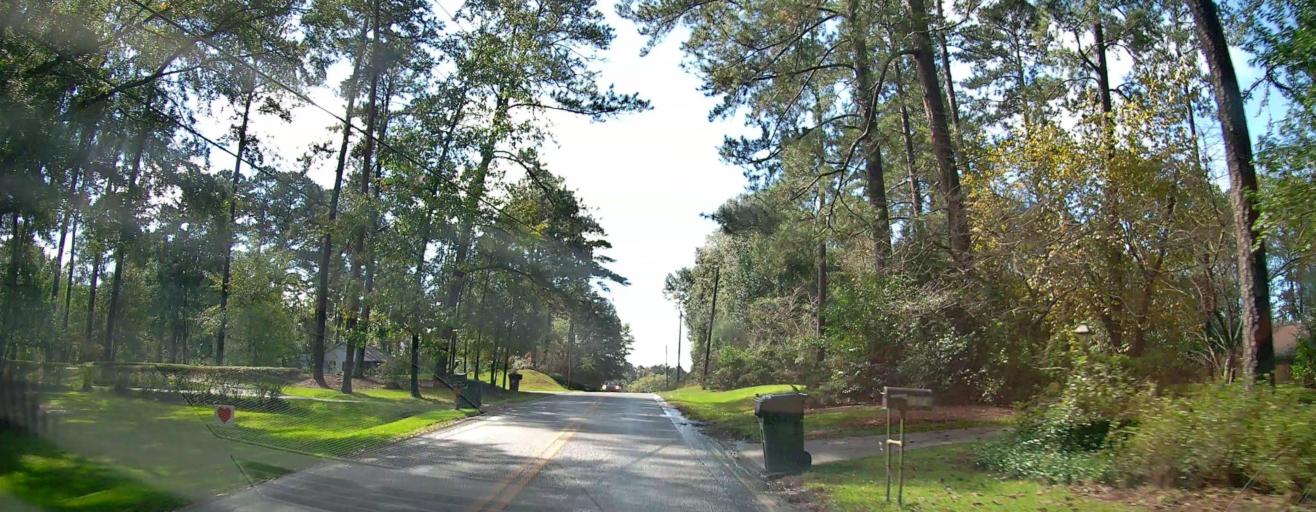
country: US
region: Georgia
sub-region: Bibb County
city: Macon
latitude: 32.9064
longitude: -83.7168
